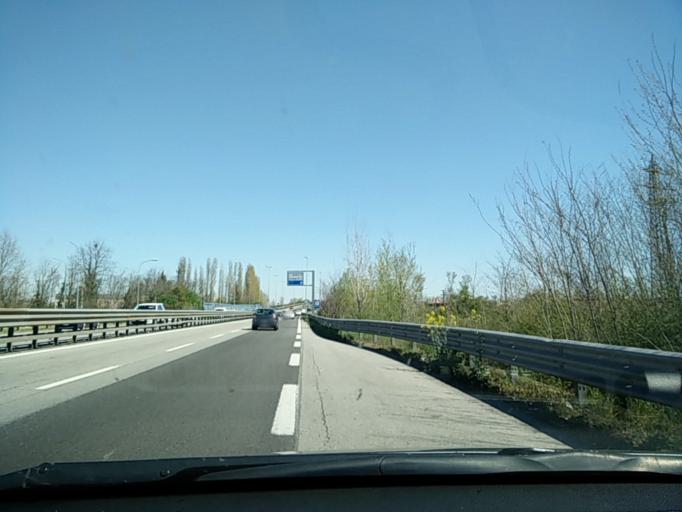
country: IT
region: Veneto
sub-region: Provincia di Padova
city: Padova
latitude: 45.4321
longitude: 11.8637
